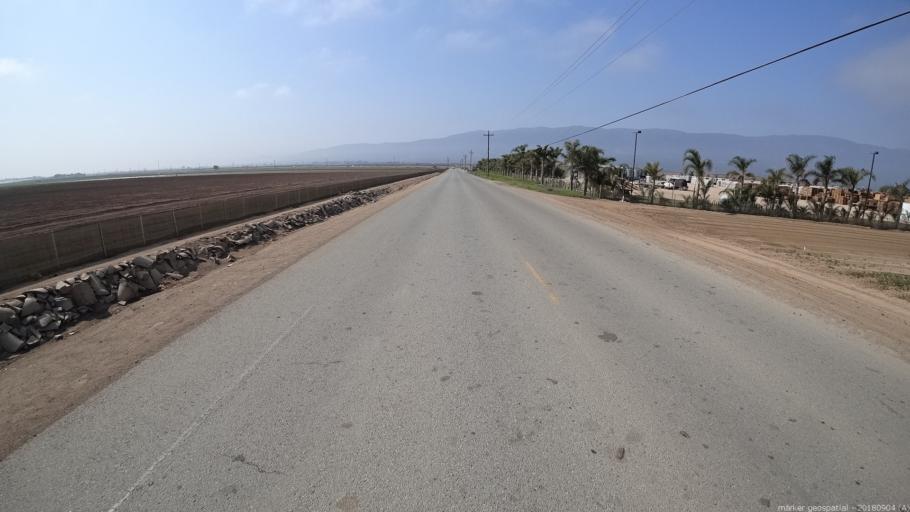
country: US
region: California
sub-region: Monterey County
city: Soledad
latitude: 36.4515
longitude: -121.3579
